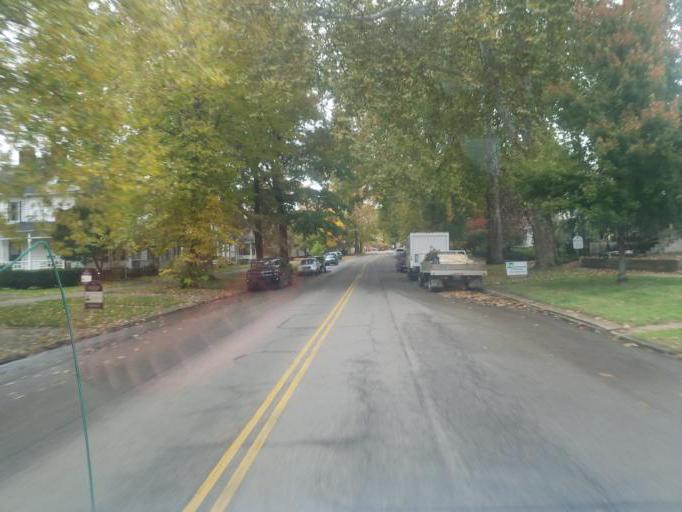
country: US
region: Ohio
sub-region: Washington County
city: Marietta
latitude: 39.4196
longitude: -81.4590
